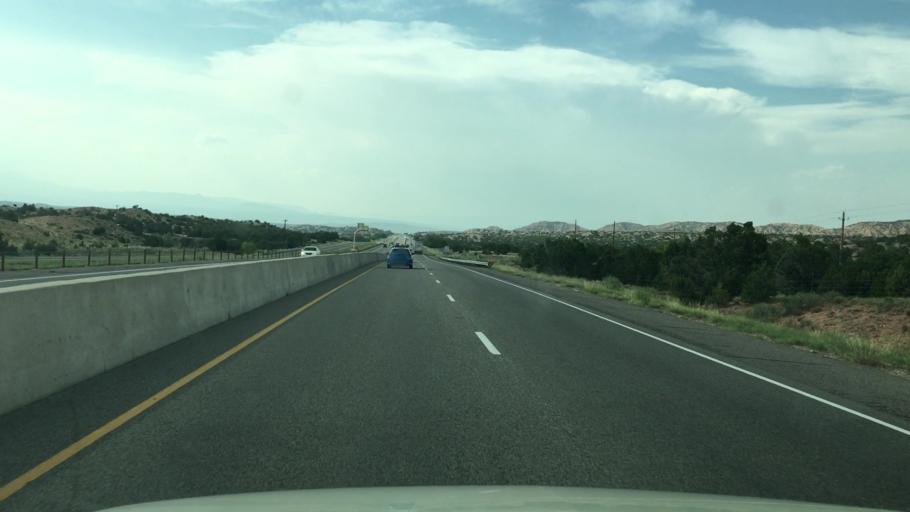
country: US
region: New Mexico
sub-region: Santa Fe County
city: Santa Fe
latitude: 35.7911
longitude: -105.9528
